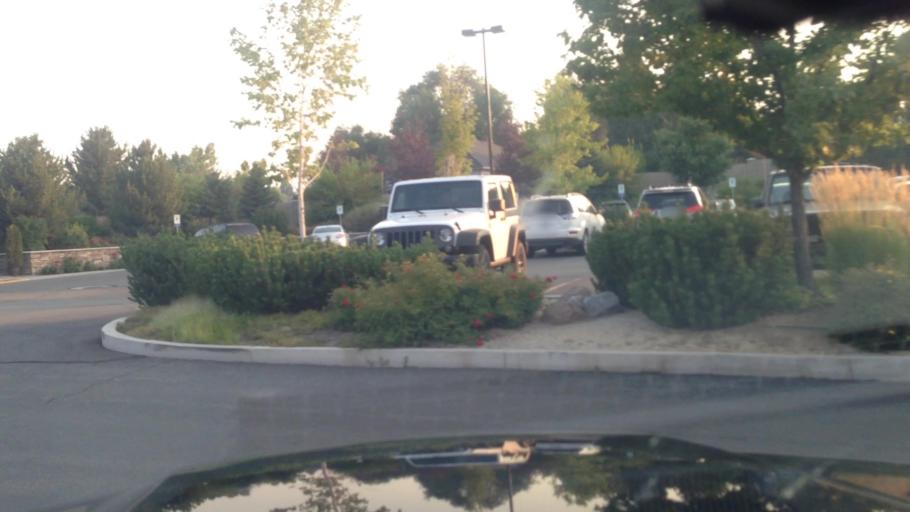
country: US
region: Nevada
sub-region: Washoe County
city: Sparks
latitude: 39.4388
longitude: -119.7716
